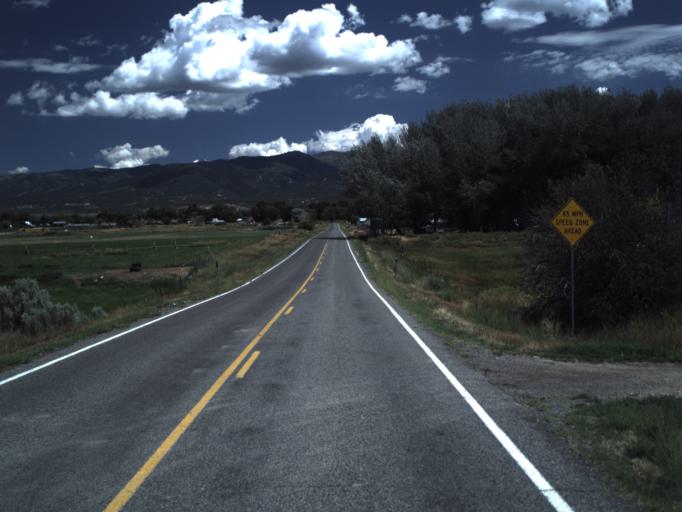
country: US
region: Utah
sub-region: Sanpete County
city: Mount Pleasant
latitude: 39.4818
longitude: -111.5088
